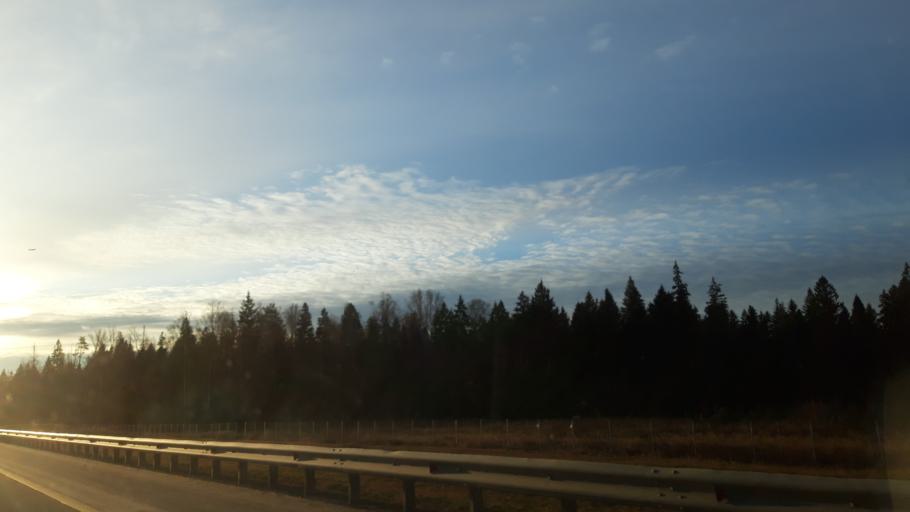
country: RU
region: Moskovskaya
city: Skhodnya
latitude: 55.9953
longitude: 37.2991
